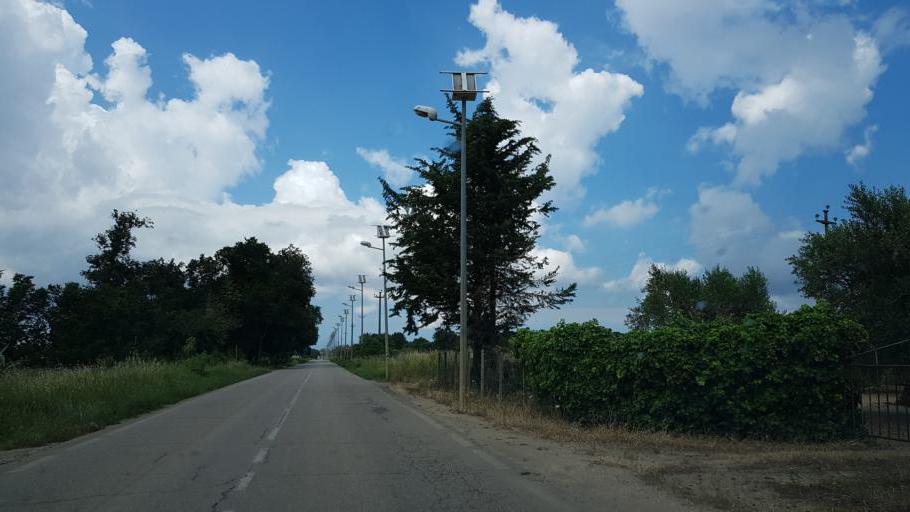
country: IT
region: Apulia
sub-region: Provincia di Brindisi
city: Tuturano
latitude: 40.5338
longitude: 17.9437
